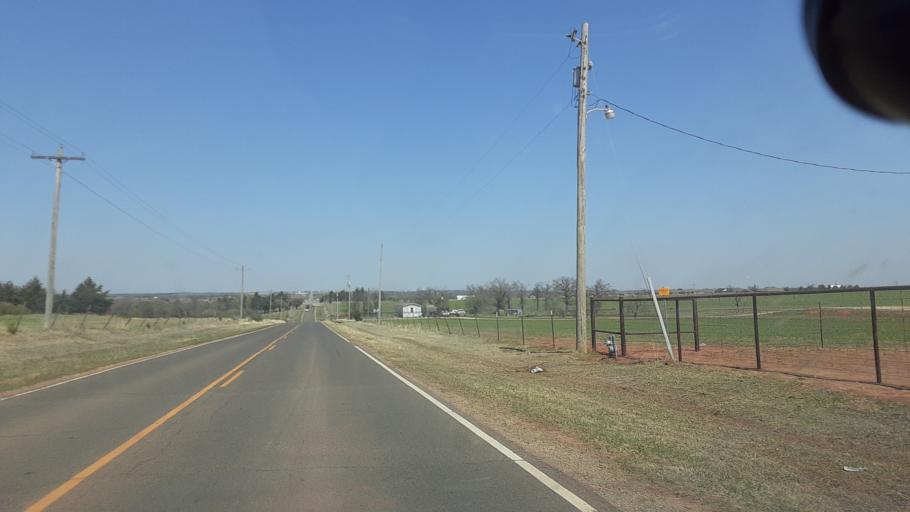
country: US
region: Oklahoma
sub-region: Logan County
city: Guthrie
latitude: 35.7928
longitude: -97.4784
